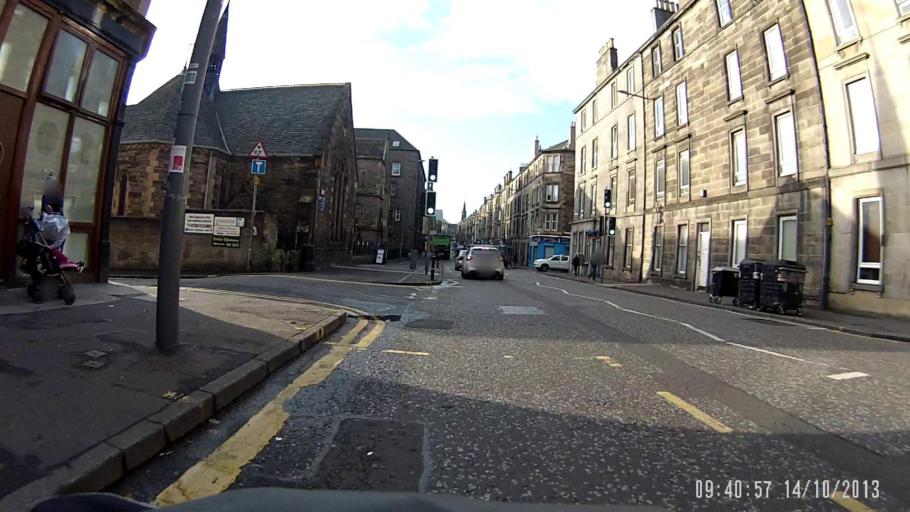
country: GB
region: Scotland
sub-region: West Lothian
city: Seafield
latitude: 55.9611
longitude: -3.1712
